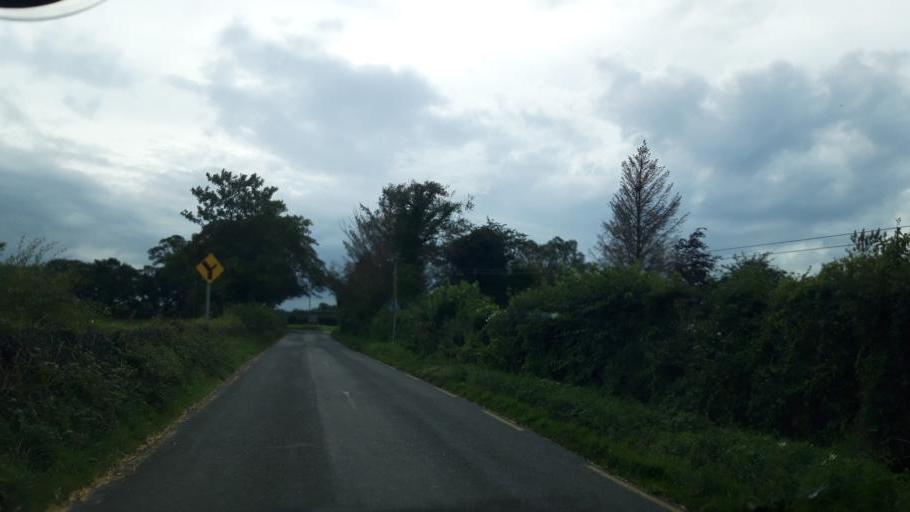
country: IE
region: Leinster
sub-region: Kilkenny
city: Ballyragget
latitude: 52.7570
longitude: -7.3888
